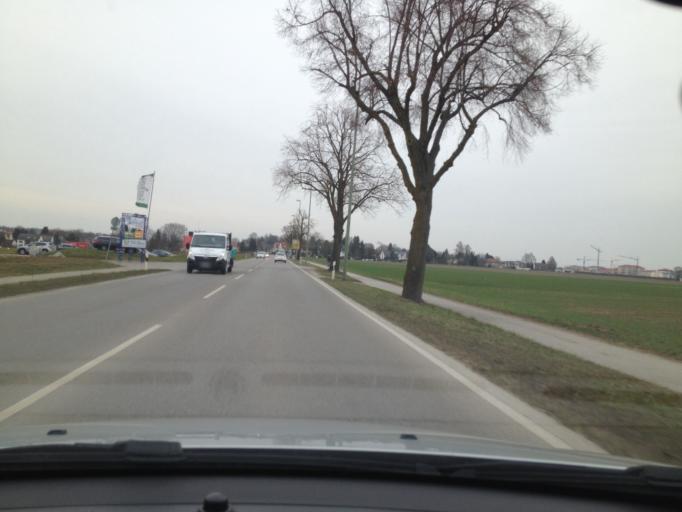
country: DE
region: Bavaria
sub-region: Swabia
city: Stadtbergen
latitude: 48.3263
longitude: 10.8647
